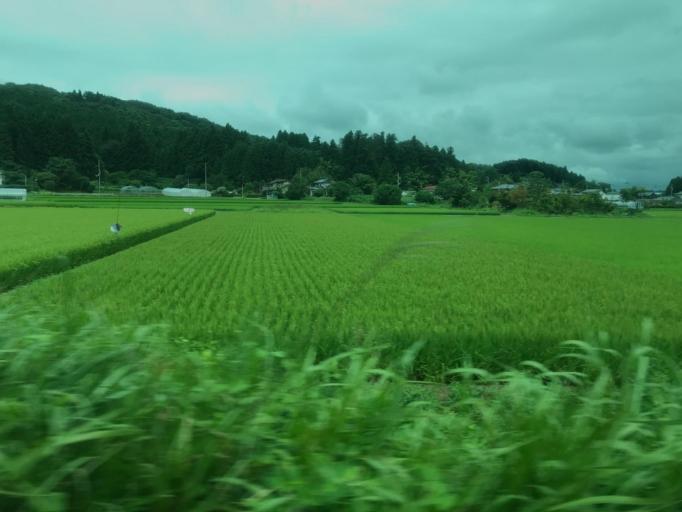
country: JP
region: Fukushima
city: Ishikawa
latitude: 37.1535
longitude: 140.2956
